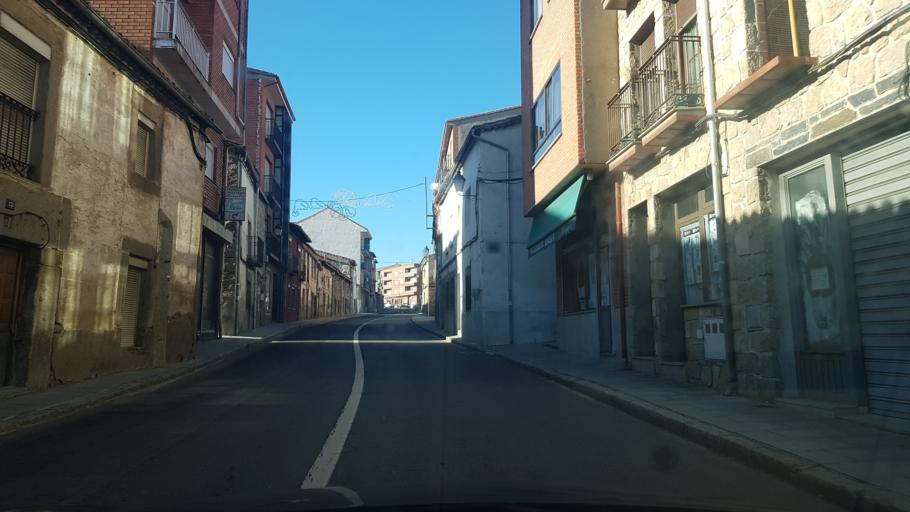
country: ES
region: Castille and Leon
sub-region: Provincia de Avila
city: Barraco
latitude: 40.4772
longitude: -4.6435
